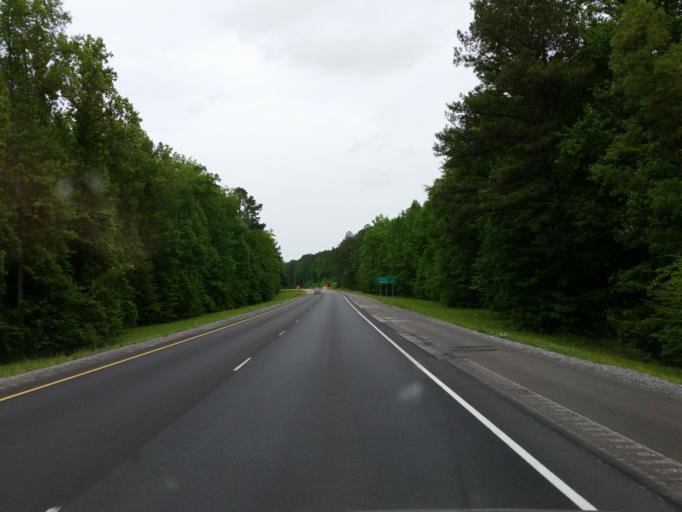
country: US
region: Mississippi
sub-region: Clarke County
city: Stonewall
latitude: 31.9725
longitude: -88.9584
